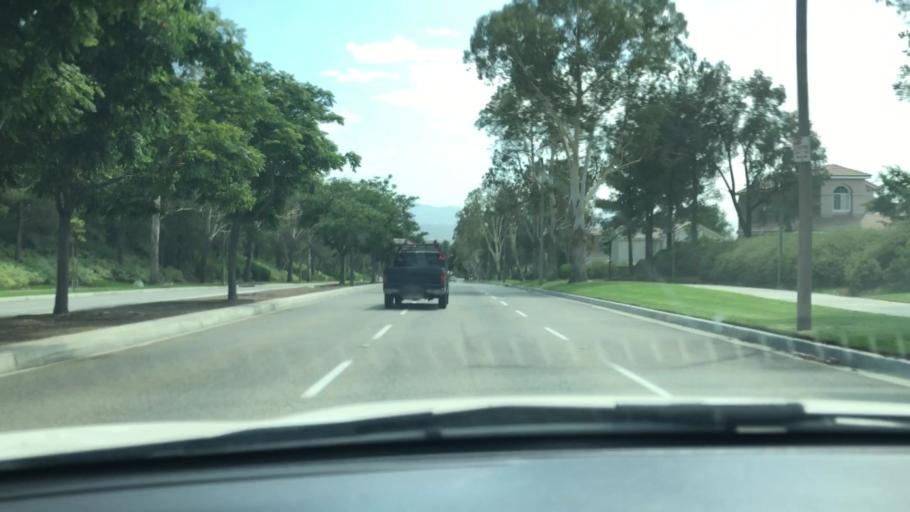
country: US
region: California
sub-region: Los Angeles County
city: Santa Clarita
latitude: 34.4506
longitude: -118.5504
